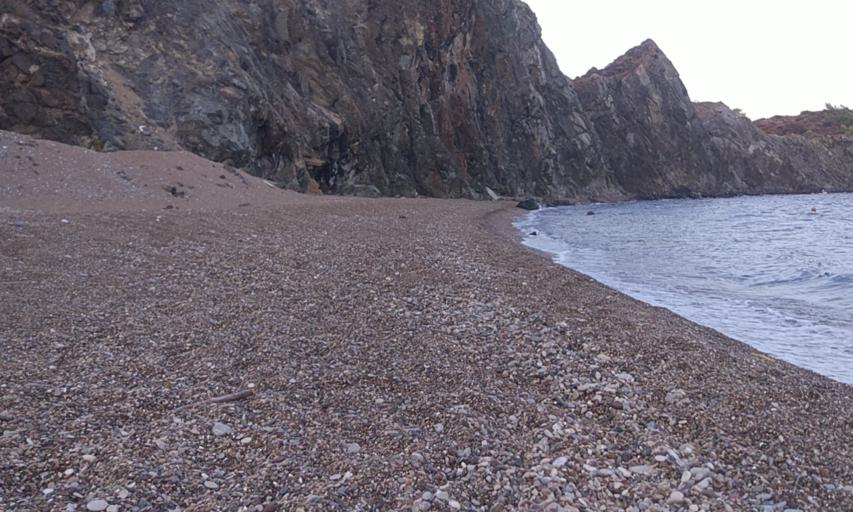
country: TR
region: Antalya
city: Tekirova
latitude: 36.4220
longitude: 30.4873
